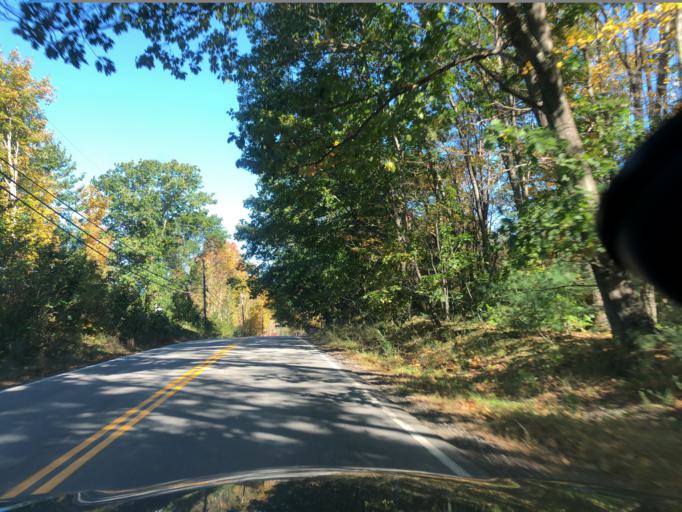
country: US
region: New Hampshire
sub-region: Rockingham County
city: Exeter
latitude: 43.0280
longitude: -70.9446
